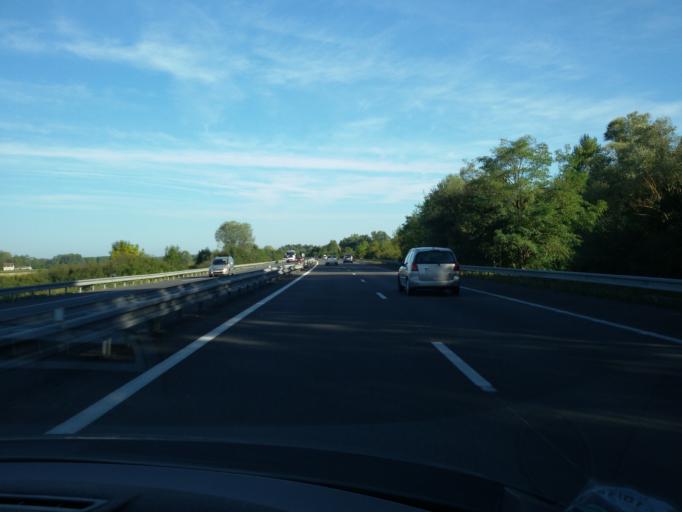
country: FR
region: Centre
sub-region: Departement du Cher
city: Foecy
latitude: 47.1796
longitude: 2.1752
